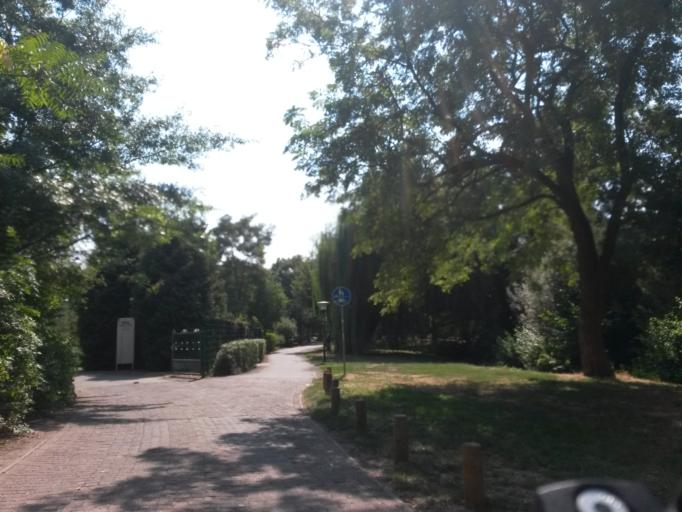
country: DE
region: Saxony-Anhalt
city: Wittenburg
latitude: 51.8751
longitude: 12.6587
